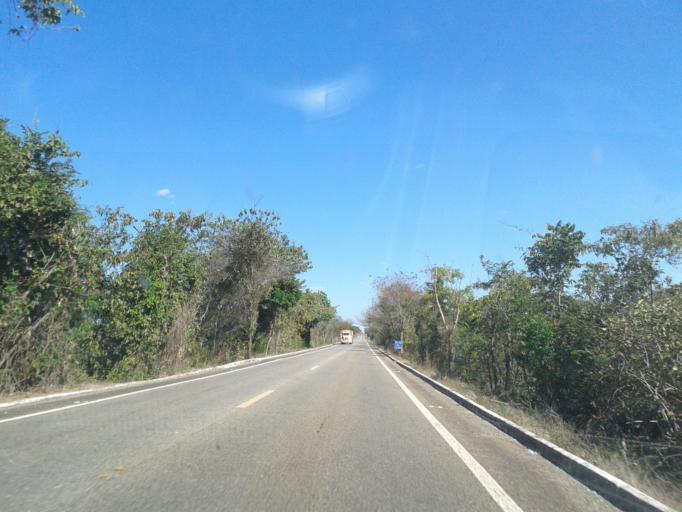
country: BR
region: Goias
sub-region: Sao Miguel Do Araguaia
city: Sao Miguel do Araguaia
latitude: -13.6864
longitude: -50.3309
